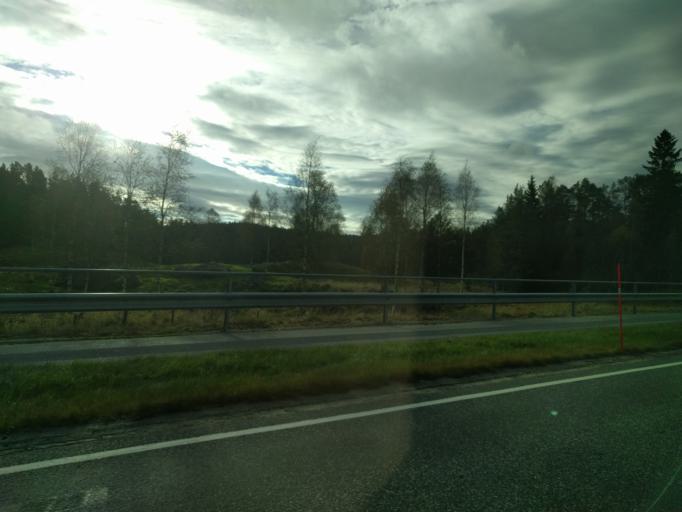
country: NO
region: Vest-Agder
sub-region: Kristiansand
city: Strai
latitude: 58.2852
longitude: 7.8421
